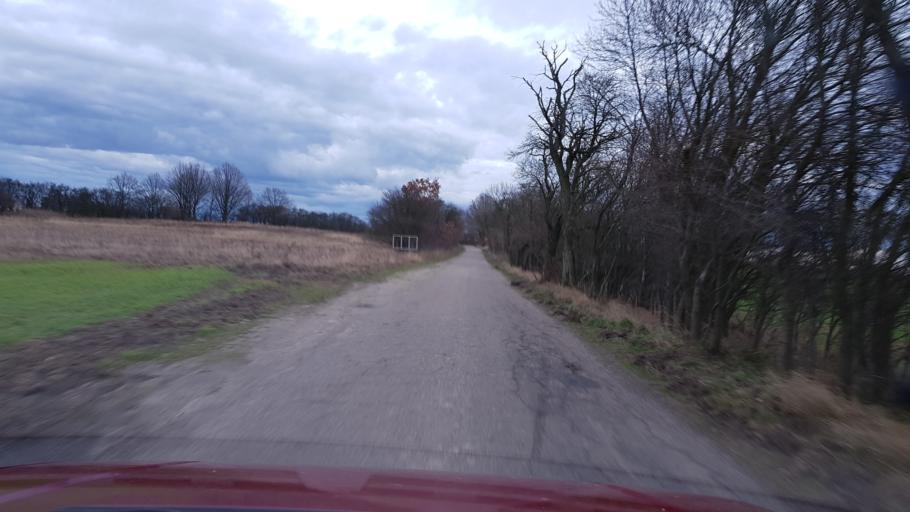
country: PL
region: West Pomeranian Voivodeship
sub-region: Powiat gryfinski
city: Stare Czarnowo
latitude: 53.3302
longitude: 14.6721
